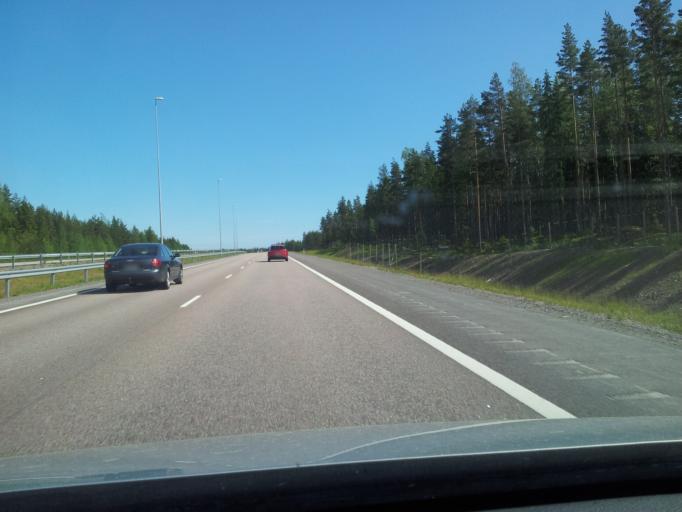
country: FI
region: Uusimaa
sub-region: Loviisa
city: Lovisa
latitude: 60.4688
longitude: 26.1285
